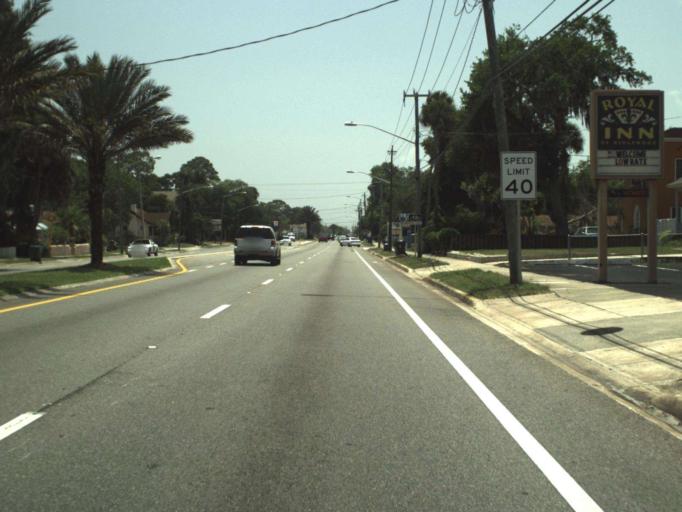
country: US
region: Florida
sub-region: Volusia County
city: Daytona Beach
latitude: 29.1966
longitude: -81.0153
